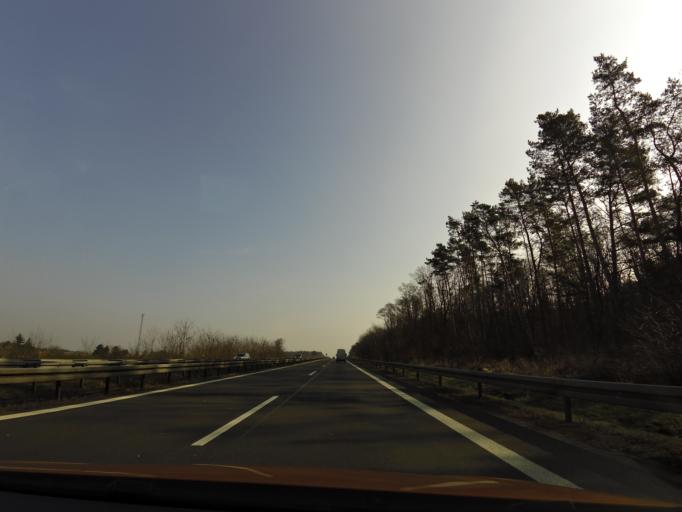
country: DE
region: Brandenburg
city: Storkow
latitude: 52.3128
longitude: 13.9258
